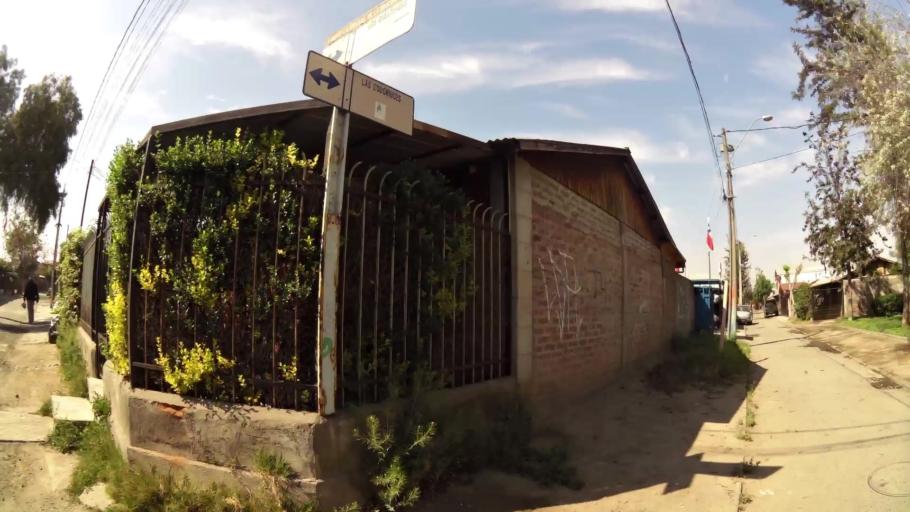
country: CL
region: Santiago Metropolitan
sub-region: Provincia de Santiago
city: La Pintana
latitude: -33.5603
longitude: -70.6552
